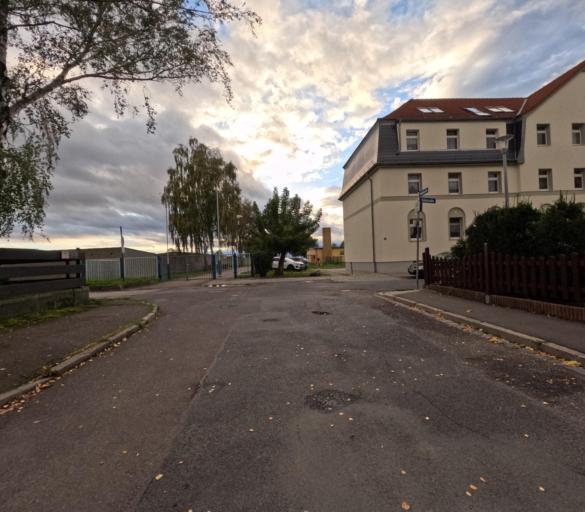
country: DE
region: Saxony
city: Markranstadt
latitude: 51.2963
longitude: 12.2226
